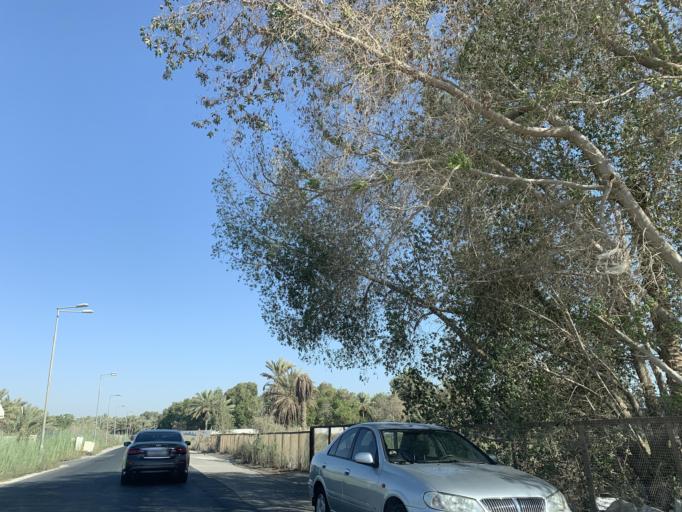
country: BH
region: Manama
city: Jidd Hafs
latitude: 26.2043
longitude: 50.4532
